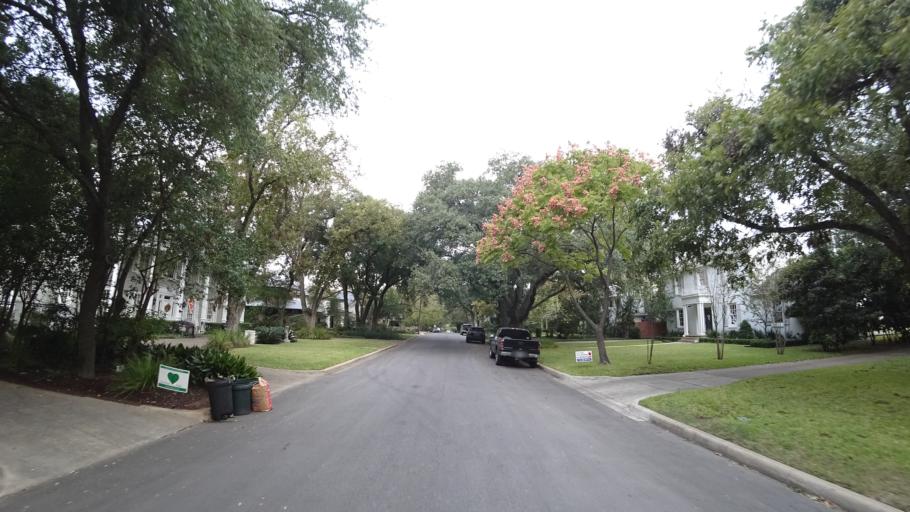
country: US
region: Texas
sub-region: Travis County
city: Austin
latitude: 30.2949
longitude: -97.7539
